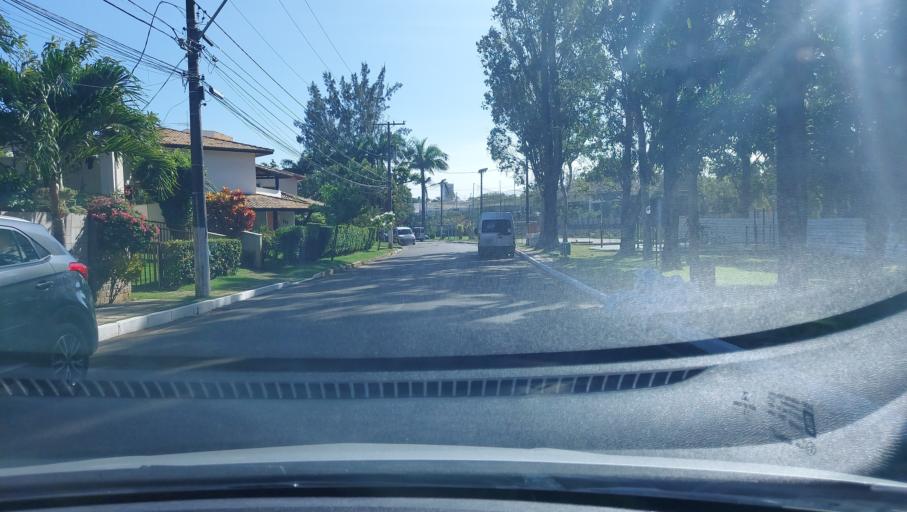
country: BR
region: Bahia
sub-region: Lauro De Freitas
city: Lauro de Freitas
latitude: -12.9411
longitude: -38.3832
